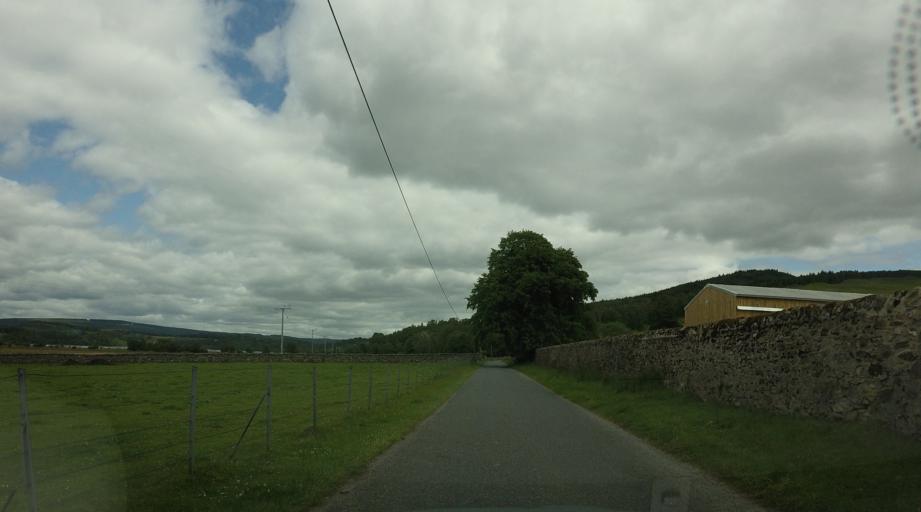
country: GB
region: Scotland
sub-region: Perth and Kinross
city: Aberfeldy
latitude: 56.6908
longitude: -4.1437
